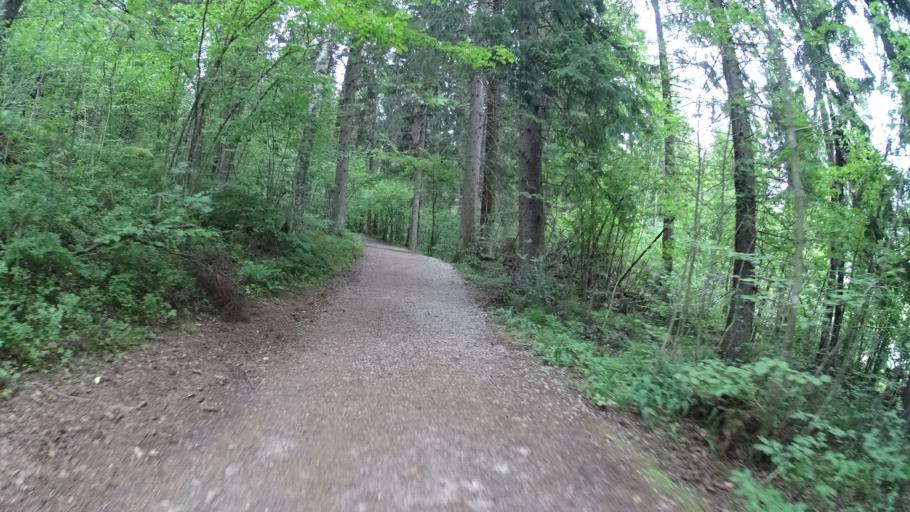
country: FI
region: Uusimaa
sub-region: Helsinki
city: Espoo
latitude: 60.2791
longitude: 24.6595
